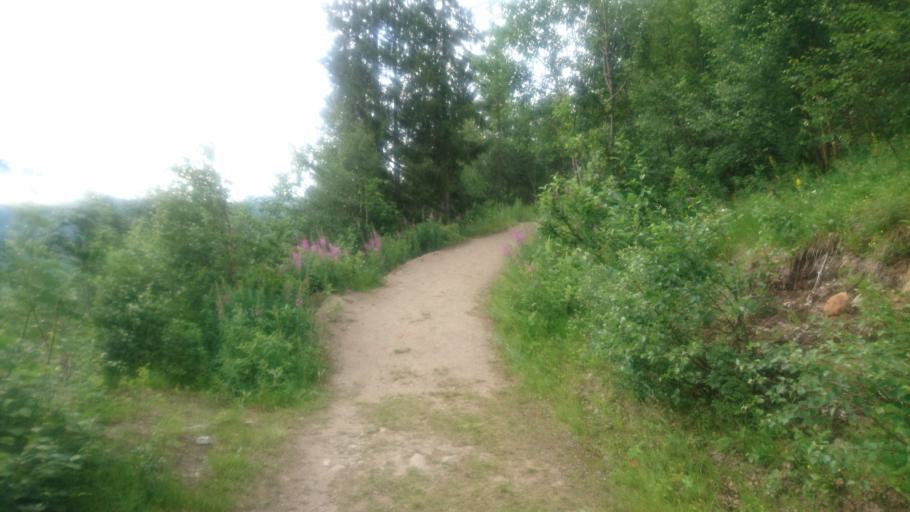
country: NO
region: Nordland
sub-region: Rana
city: Mo i Rana
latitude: 66.4148
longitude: 14.2636
